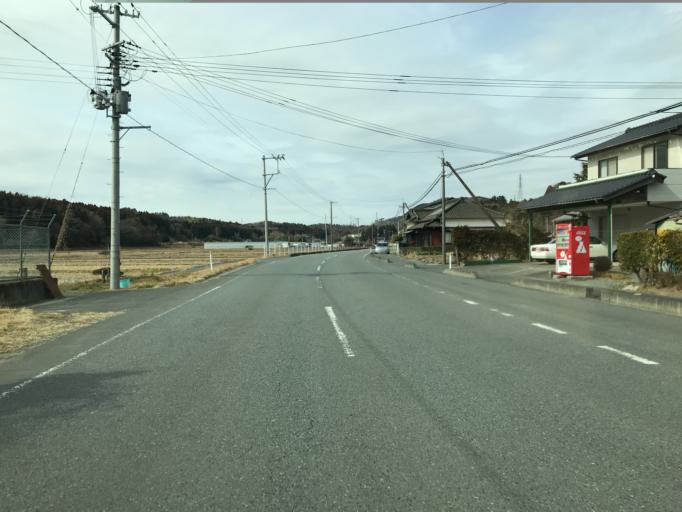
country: JP
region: Fukushima
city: Iwaki
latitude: 37.1178
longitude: 140.9467
